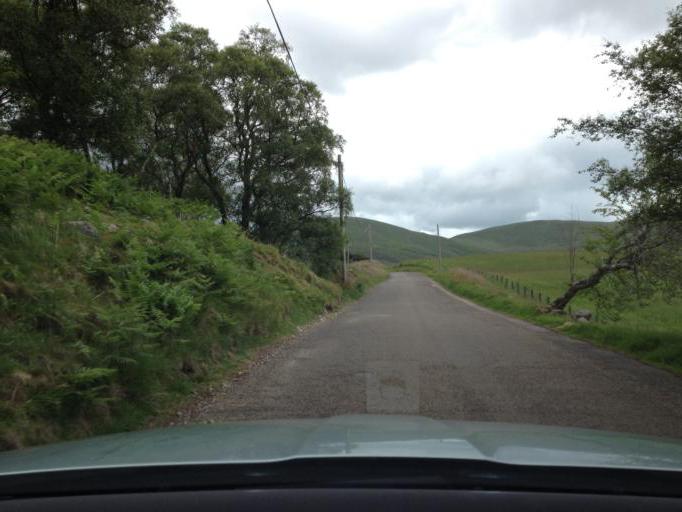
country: GB
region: Scotland
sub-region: Aberdeenshire
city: Aboyne
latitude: 56.8921
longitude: -2.7824
